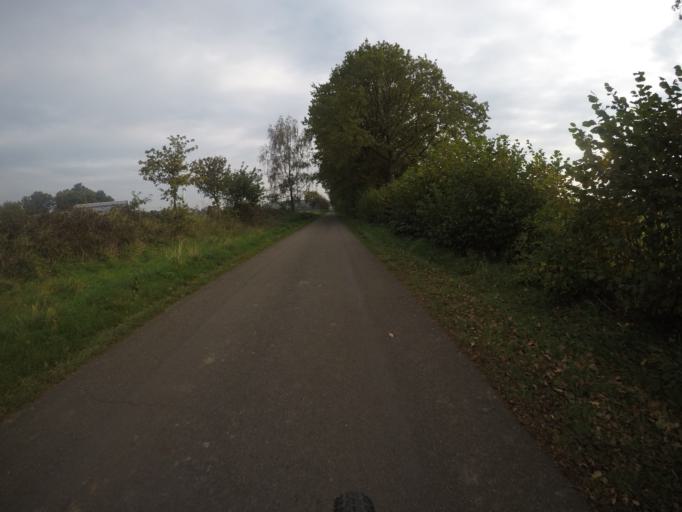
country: DE
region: North Rhine-Westphalia
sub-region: Regierungsbezirk Munster
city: Isselburg
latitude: 51.8308
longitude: 6.5096
